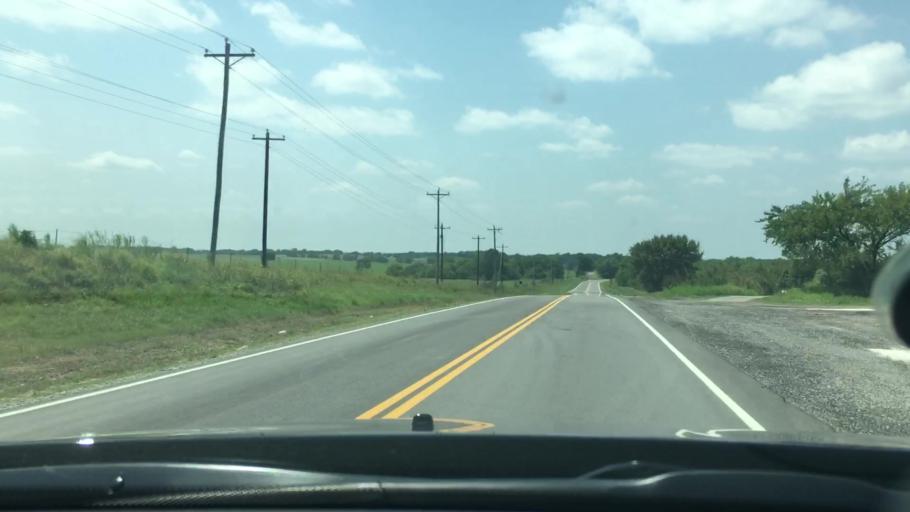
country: US
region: Oklahoma
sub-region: Atoka County
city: Atoka
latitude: 34.3749
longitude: -96.2531
